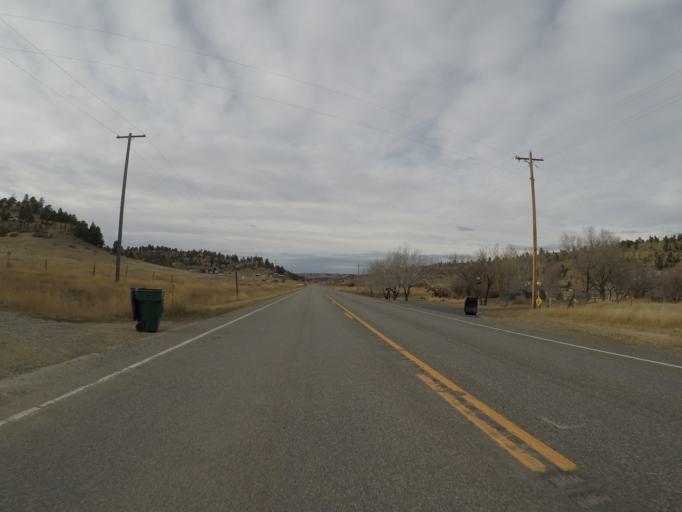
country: US
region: Montana
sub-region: Yellowstone County
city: Laurel
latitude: 45.8177
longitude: -108.6937
